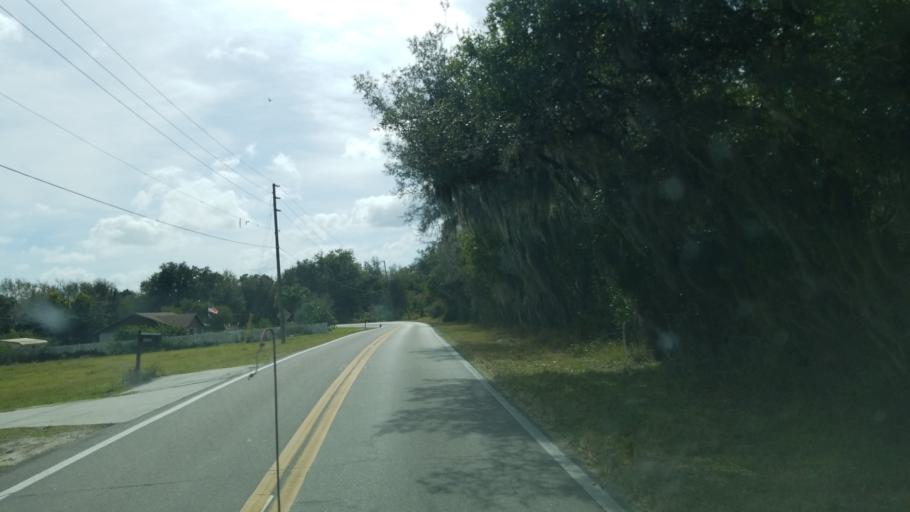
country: US
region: Florida
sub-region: Polk County
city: Lake Wales
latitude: 27.9651
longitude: -81.5405
